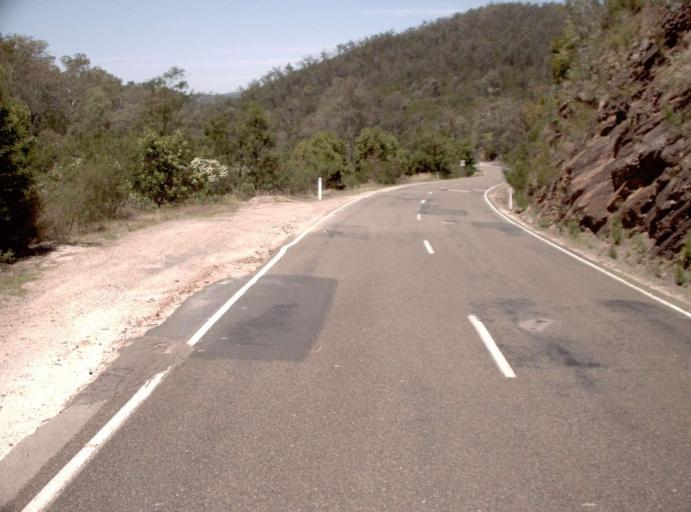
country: AU
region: Victoria
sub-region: East Gippsland
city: Bairnsdale
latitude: -37.4795
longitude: 147.8301
